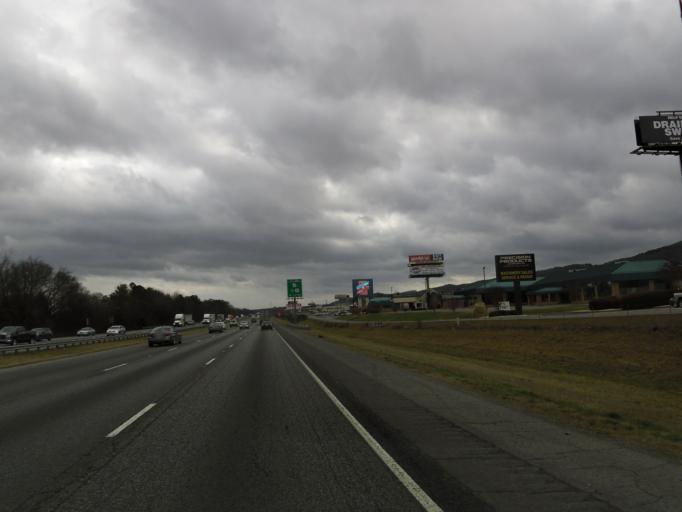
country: US
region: Georgia
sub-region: Whitfield County
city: Dalton
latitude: 34.6974
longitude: -85.0050
